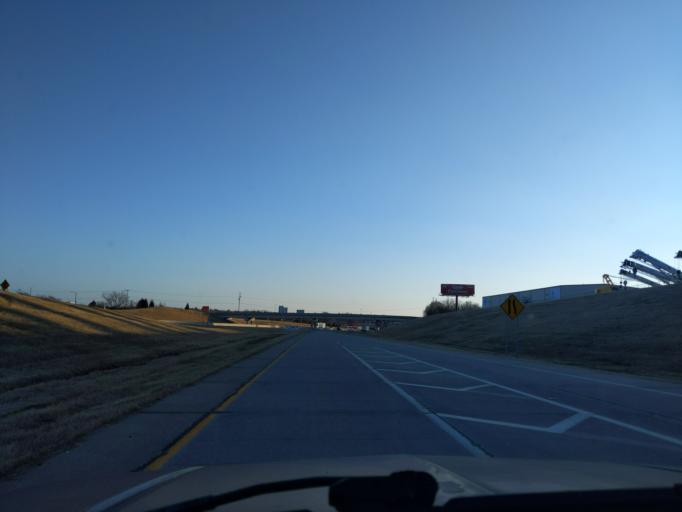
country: US
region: Oklahoma
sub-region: Creek County
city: Sapulpa
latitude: 36.0273
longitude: -96.0938
